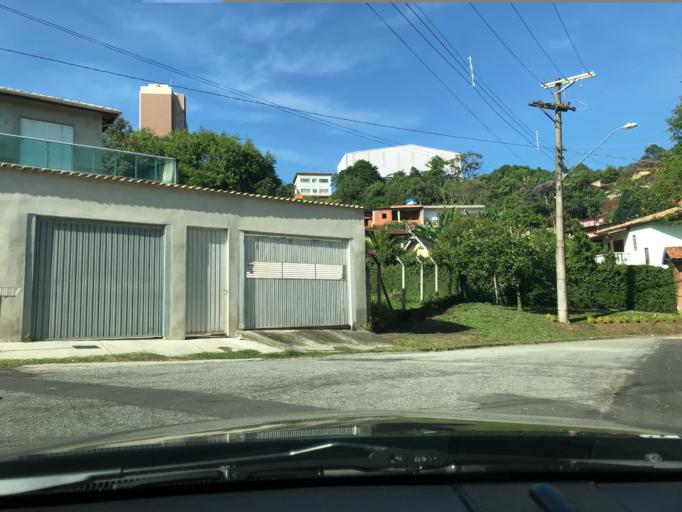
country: BR
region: Sao Paulo
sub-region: Itapevi
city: Itapevi
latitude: -23.5358
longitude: -46.9431
